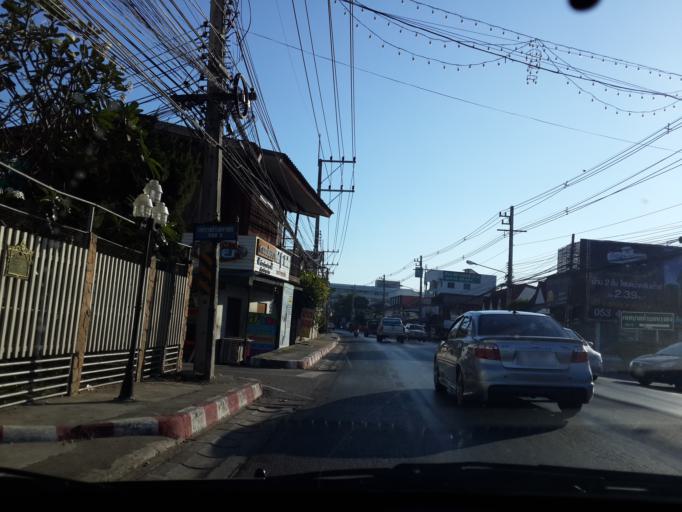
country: TH
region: Chiang Mai
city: Hang Dong
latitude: 18.6864
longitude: 98.9194
